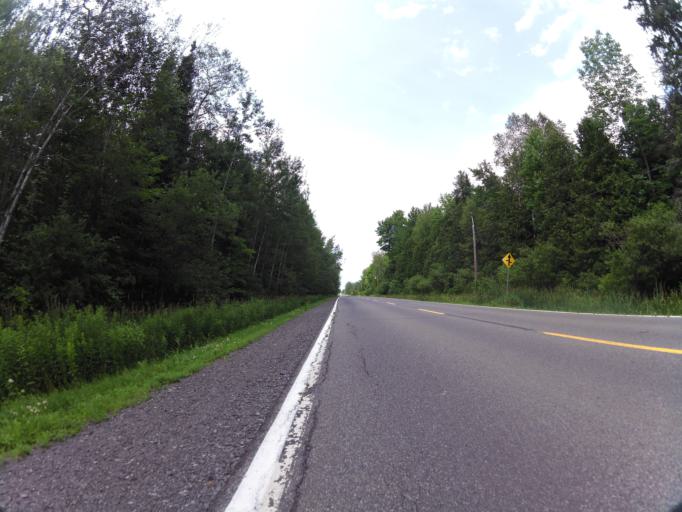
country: CA
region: Ontario
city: Ottawa
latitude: 45.2022
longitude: -75.5926
